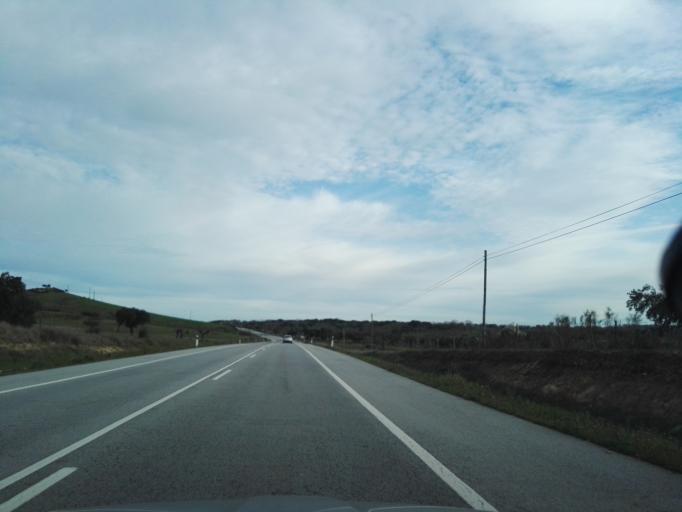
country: PT
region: Portalegre
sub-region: Portalegre
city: Urra
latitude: 39.2547
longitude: -7.4074
